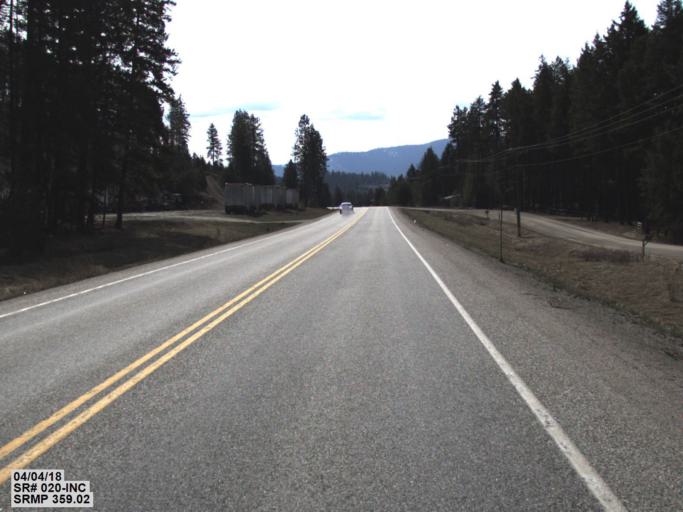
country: US
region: Washington
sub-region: Stevens County
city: Colville
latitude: 48.5284
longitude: -117.8201
